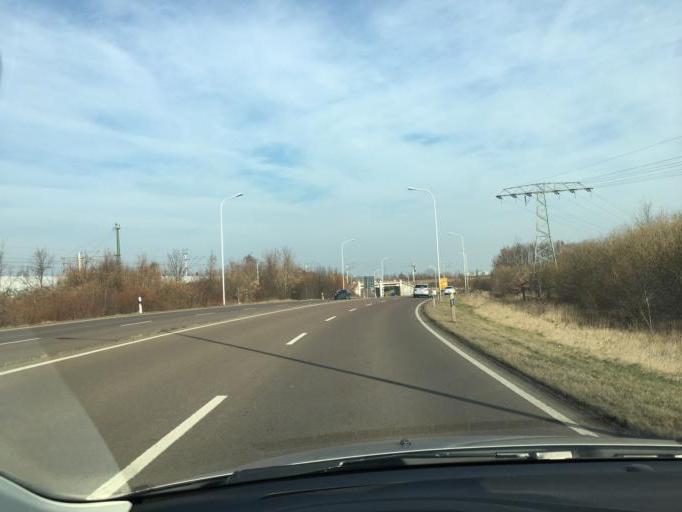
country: DE
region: Saxony-Anhalt
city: Halle (Saale)
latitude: 51.4610
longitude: 11.9959
